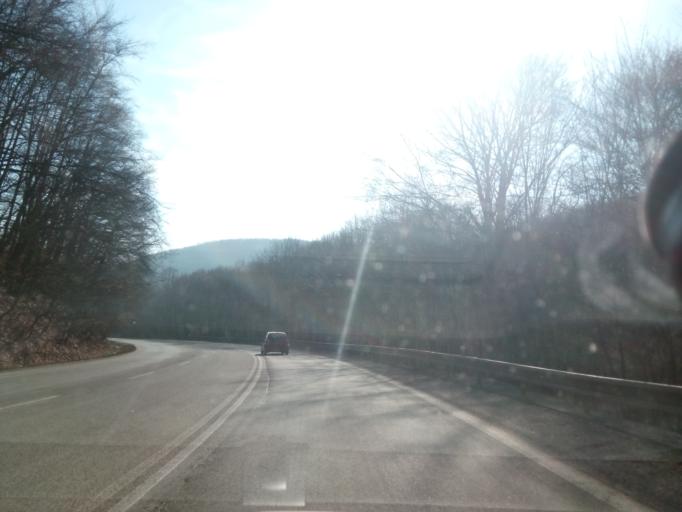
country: SK
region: Kosicky
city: Secovce
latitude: 48.7358
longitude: 21.5444
